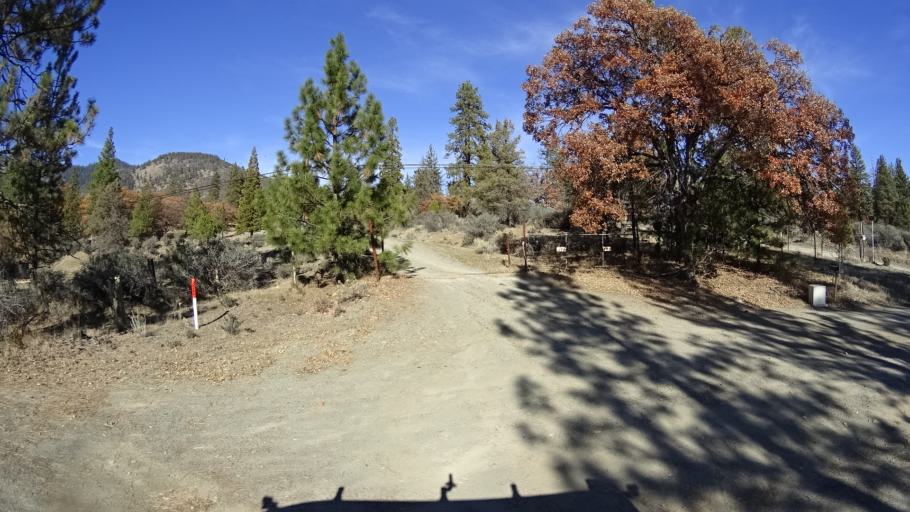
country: US
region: California
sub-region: Siskiyou County
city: Yreka
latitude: 41.7206
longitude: -122.6886
